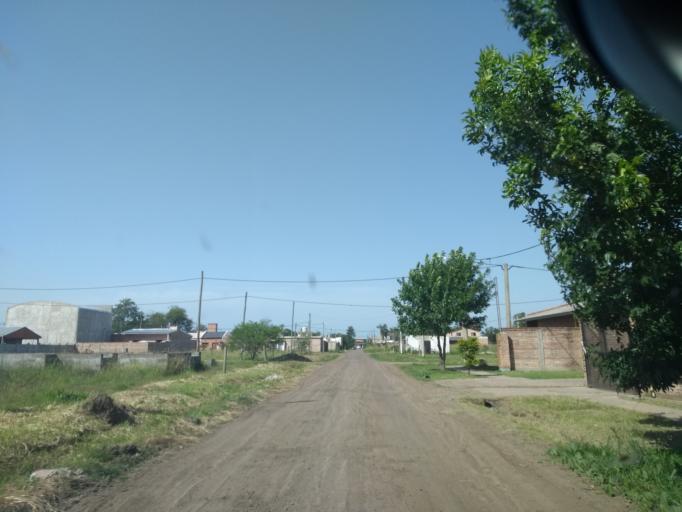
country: AR
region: Chaco
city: Fontana
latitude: -27.4147
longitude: -59.0361
